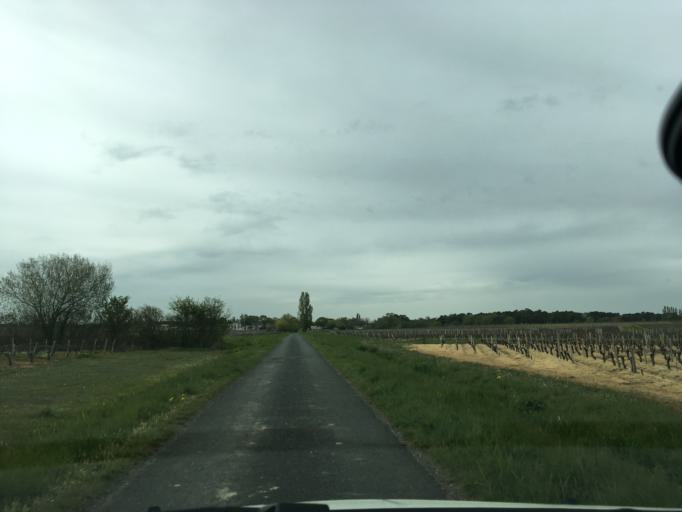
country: FR
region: Aquitaine
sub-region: Departement de la Gironde
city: Lesparre-Medoc
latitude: 45.3196
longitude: -0.8952
